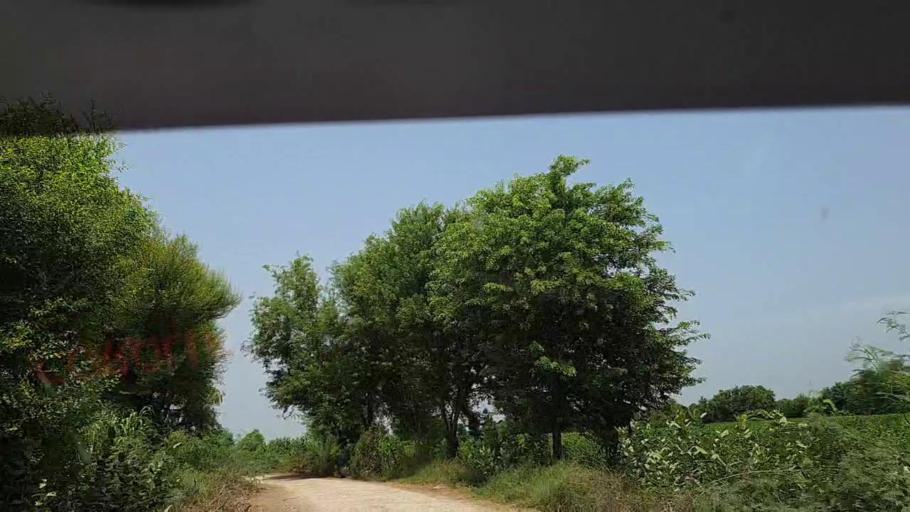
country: PK
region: Sindh
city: Adilpur
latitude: 27.8814
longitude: 69.2607
